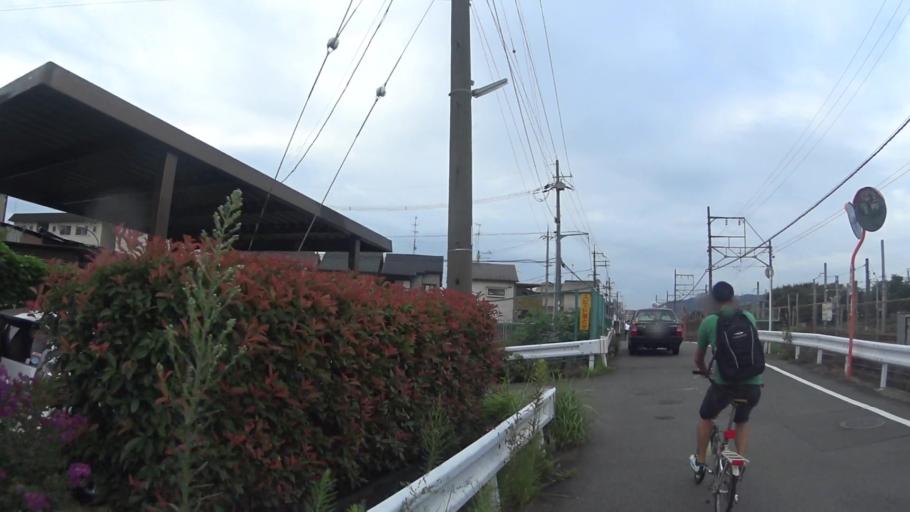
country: JP
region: Kyoto
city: Muko
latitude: 34.9249
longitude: 135.7030
